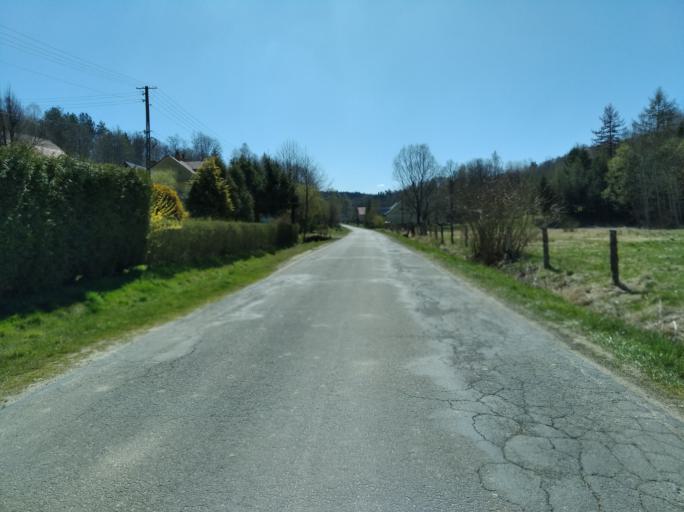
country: PL
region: Subcarpathian Voivodeship
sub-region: Powiat brzozowski
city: Jablonka
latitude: 49.7339
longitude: 22.1454
